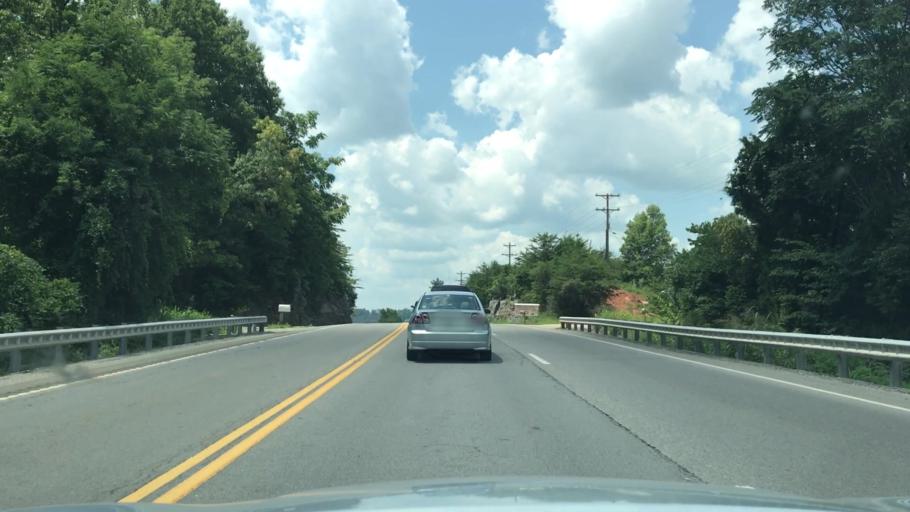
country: US
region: Tennessee
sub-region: Overton County
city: Livingston
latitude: 36.4364
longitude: -85.2743
